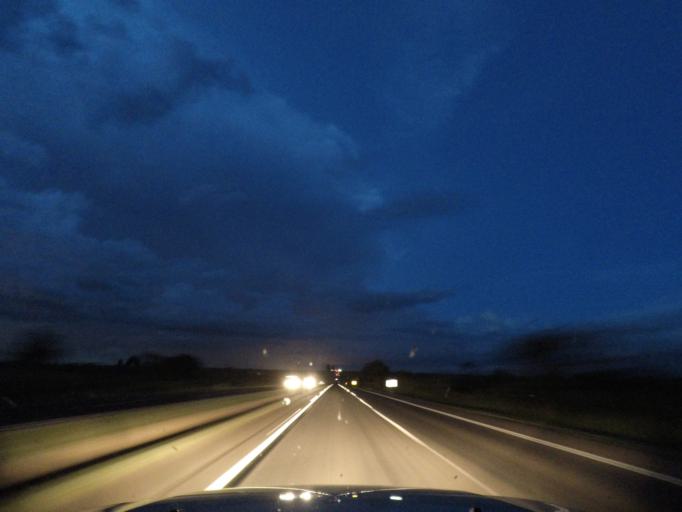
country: BR
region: Minas Gerais
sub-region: Uberlandia
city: Uberlandia
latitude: -19.2078
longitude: -48.1494
